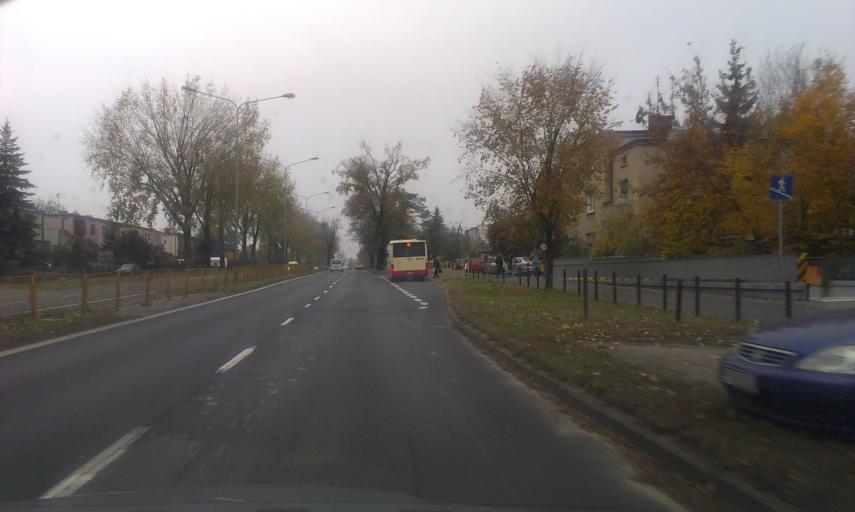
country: PL
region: Greater Poland Voivodeship
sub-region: Powiat poznanski
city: Suchy Las
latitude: 52.4274
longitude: 16.8556
